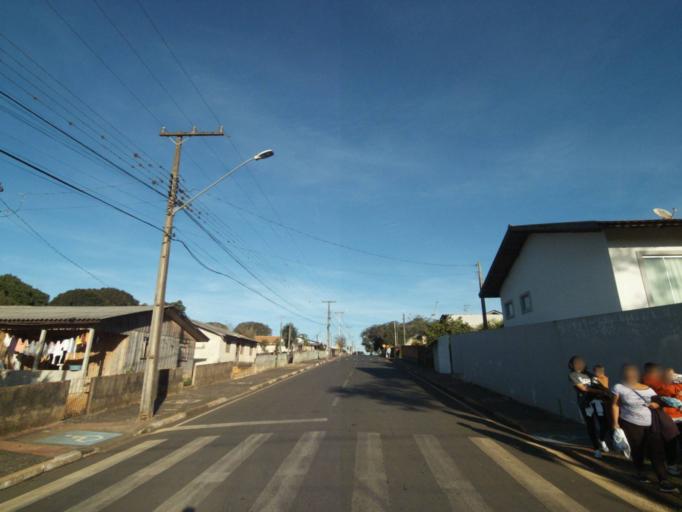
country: BR
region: Parana
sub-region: Tibagi
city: Tibagi
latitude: -24.5195
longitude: -50.4065
